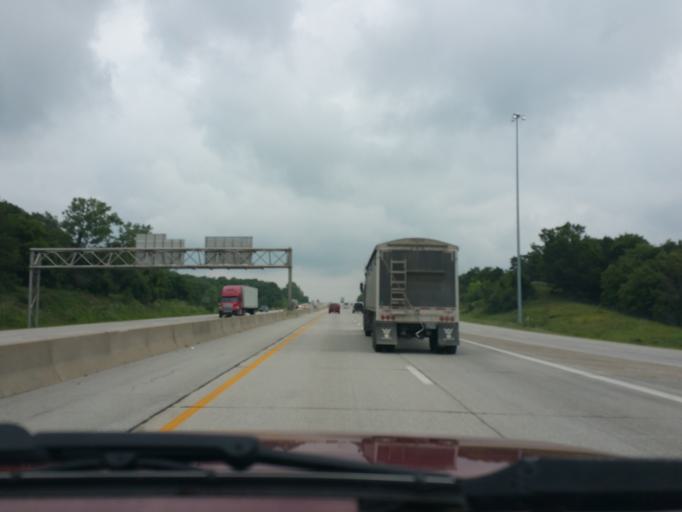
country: US
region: Kansas
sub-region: Wyandotte County
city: Edwardsville
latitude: 39.1059
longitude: -94.8019
